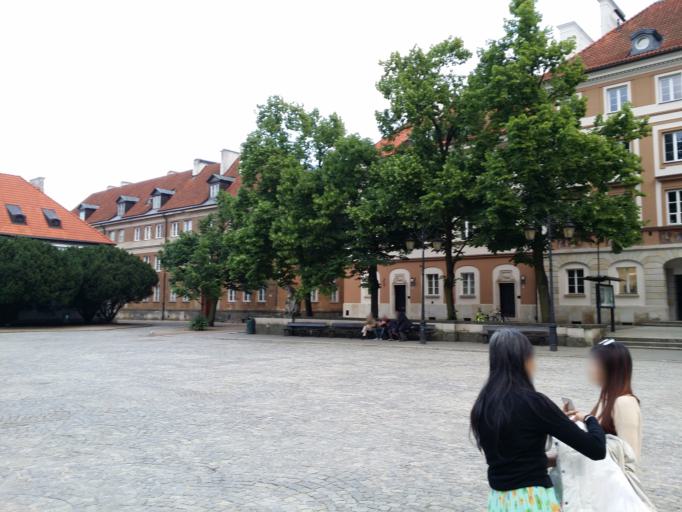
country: PL
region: Masovian Voivodeship
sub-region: Warszawa
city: Wola
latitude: 52.2529
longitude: 21.0081
